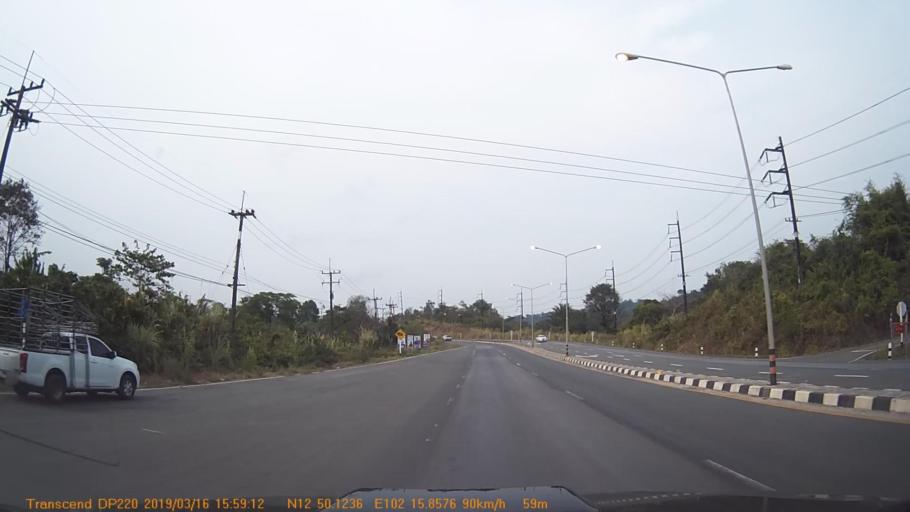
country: TH
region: Chanthaburi
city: Pong Nam Ron
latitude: 12.8358
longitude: 102.2644
